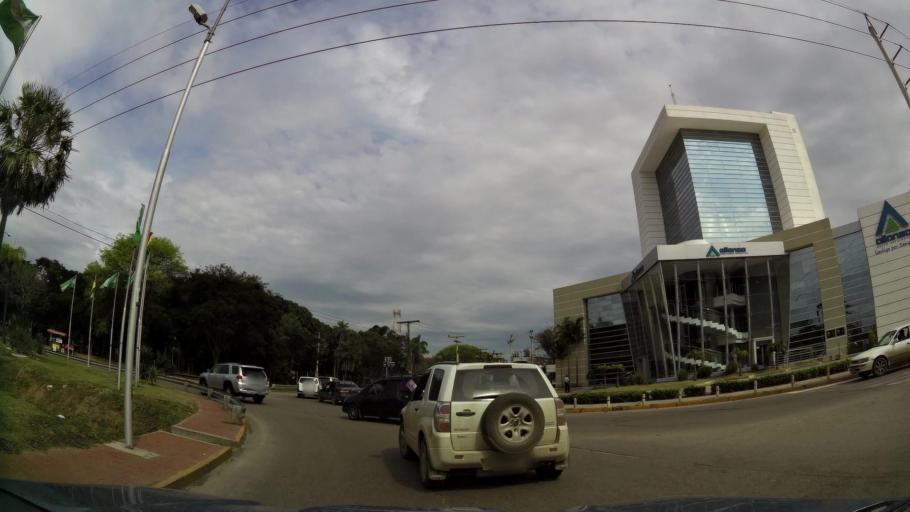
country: BO
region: Santa Cruz
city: Santa Cruz de la Sierra
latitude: -17.7855
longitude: -63.2067
